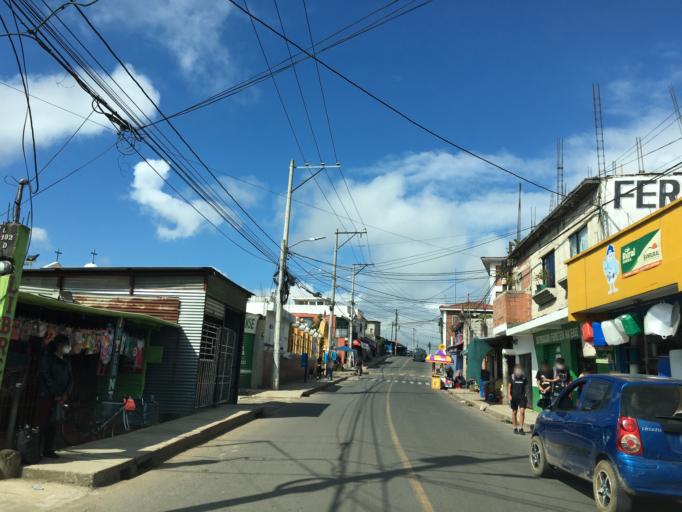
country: GT
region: Guatemala
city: San Jose Pinula
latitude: 14.5494
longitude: -90.4383
